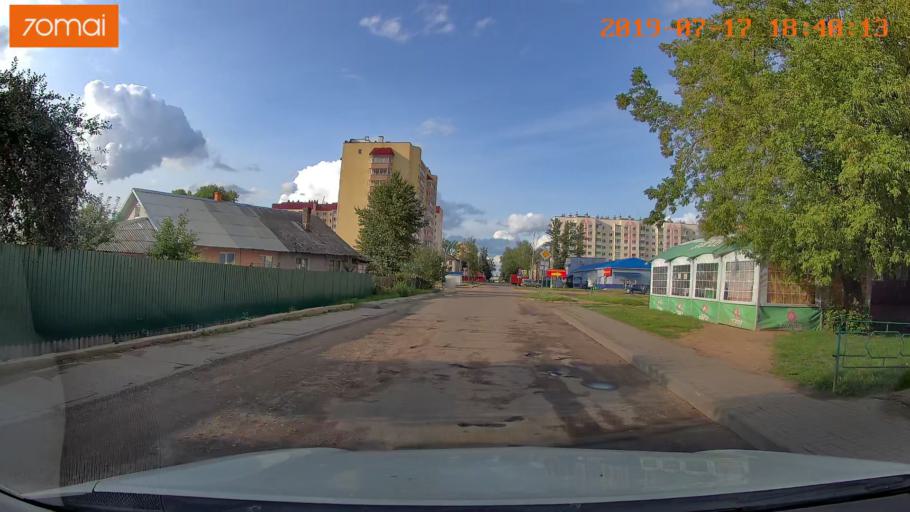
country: BY
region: Mogilev
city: Asipovichy
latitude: 53.3015
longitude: 28.6541
